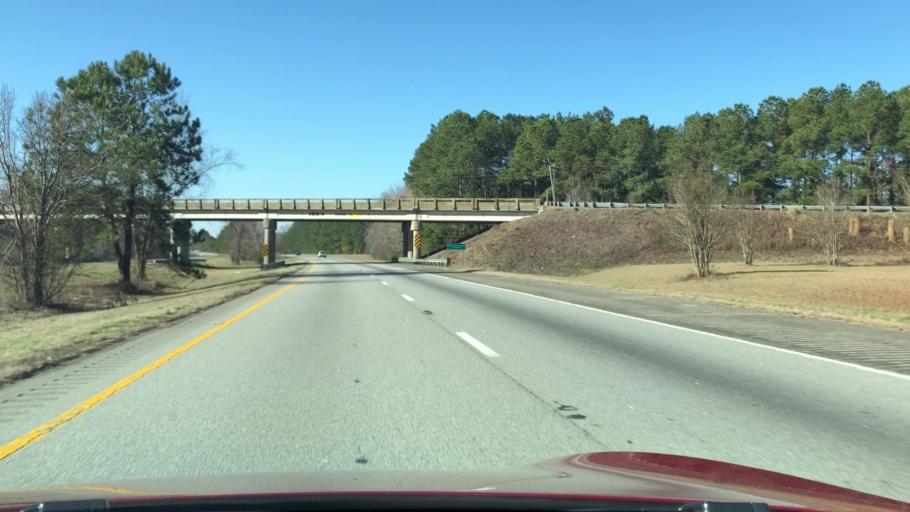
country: US
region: South Carolina
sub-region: Clarendon County
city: Manning
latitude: 33.5899
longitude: -80.3558
